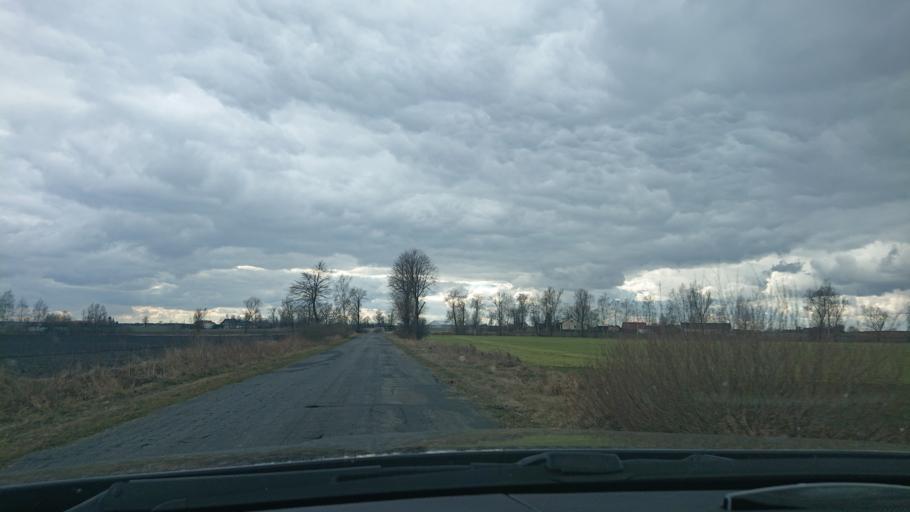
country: PL
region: Greater Poland Voivodeship
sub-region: Powiat gnieznienski
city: Niechanowo
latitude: 52.5866
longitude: 17.6943
